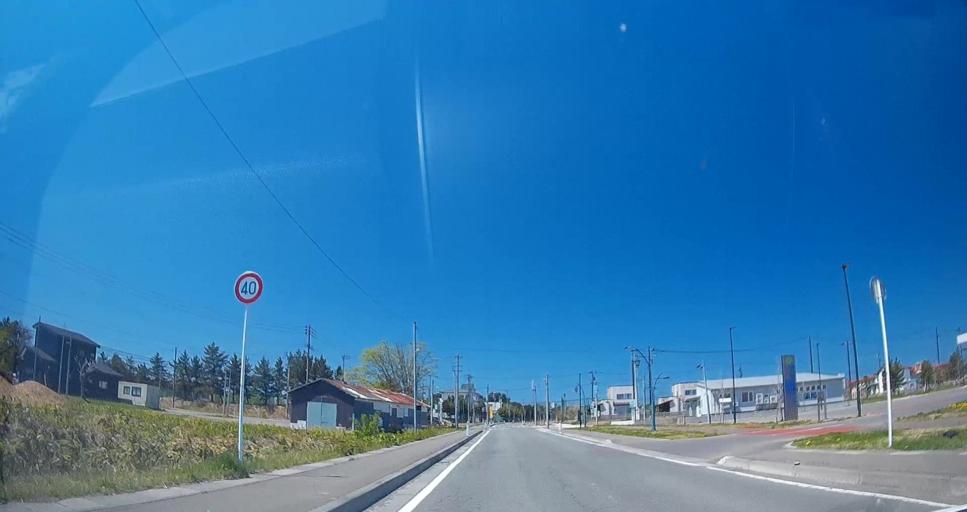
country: JP
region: Aomori
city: Misawa
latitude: 40.9690
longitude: 141.3695
